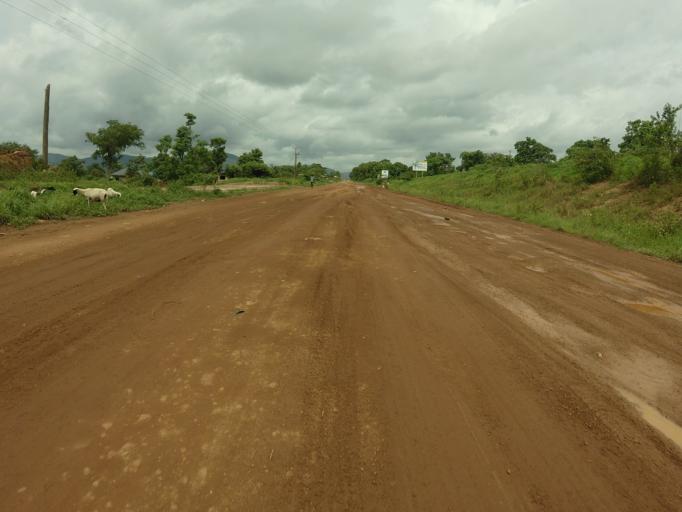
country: TG
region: Centrale
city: Sotouboua
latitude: 8.2773
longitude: 0.5094
